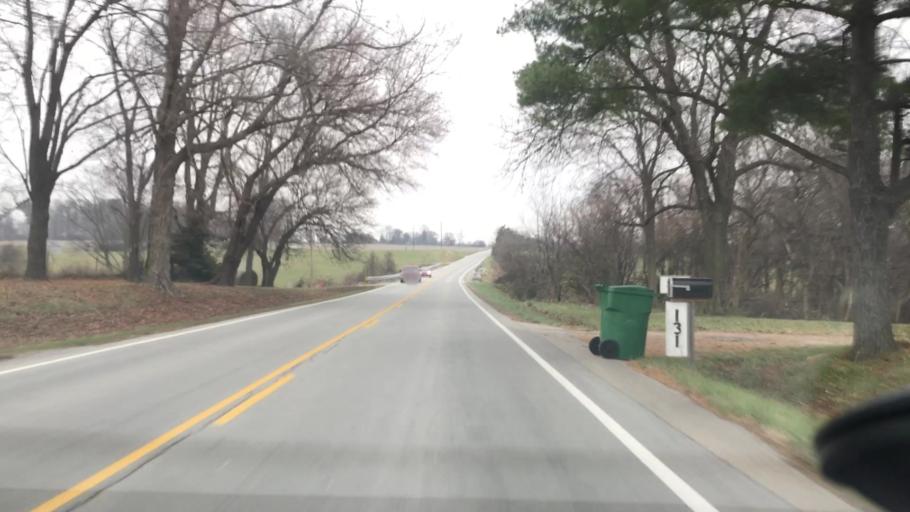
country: US
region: Ohio
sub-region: Greene County
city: Yellow Springs
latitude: 39.7987
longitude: -83.9232
